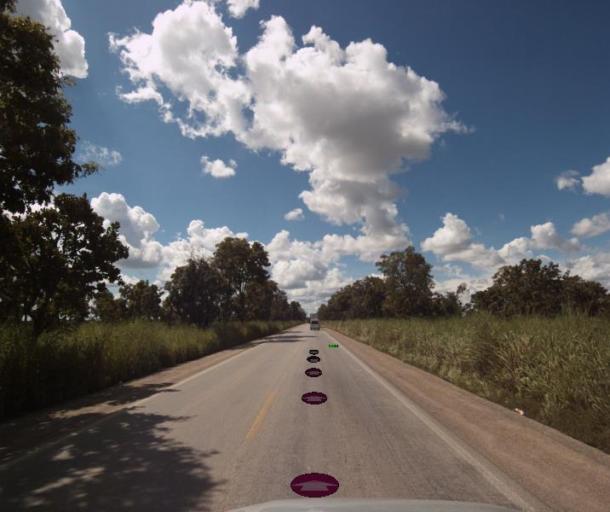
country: BR
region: Goias
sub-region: Porangatu
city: Porangatu
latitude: -13.6128
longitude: -49.0423
